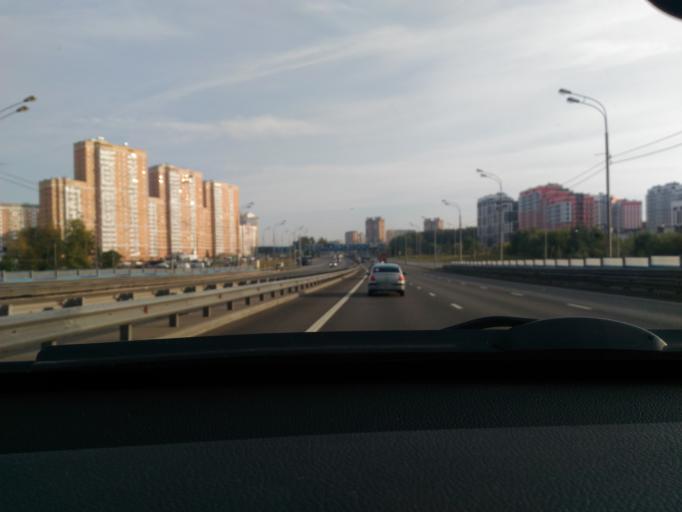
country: RU
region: Moscow
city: Severnyy
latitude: 55.9215
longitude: 37.5450
